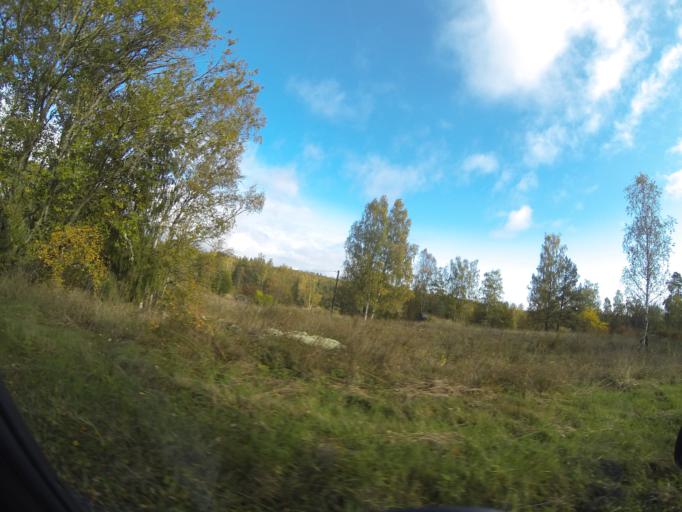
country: SE
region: Soedermanland
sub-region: Eskilstuna Kommun
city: Kvicksund
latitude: 59.3947
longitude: 16.2367
